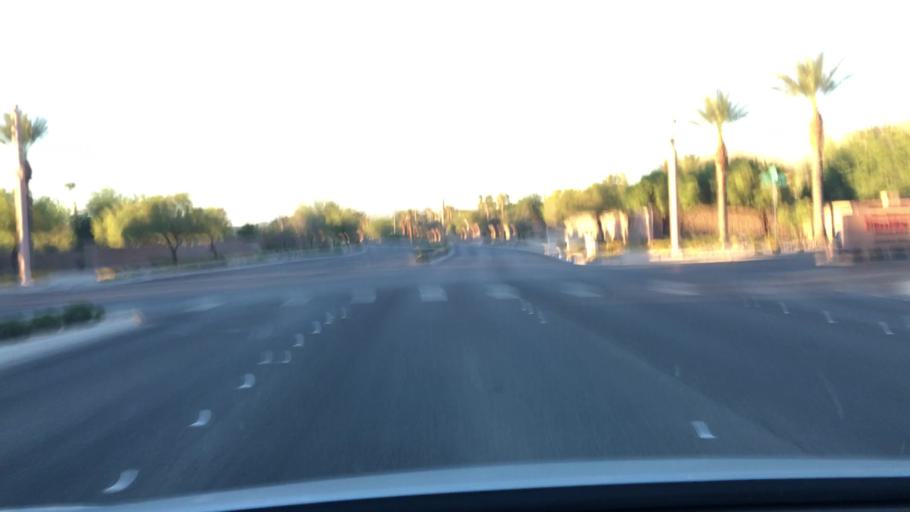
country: US
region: Nevada
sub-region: Clark County
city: Summerlin South
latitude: 36.1349
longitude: -115.3425
